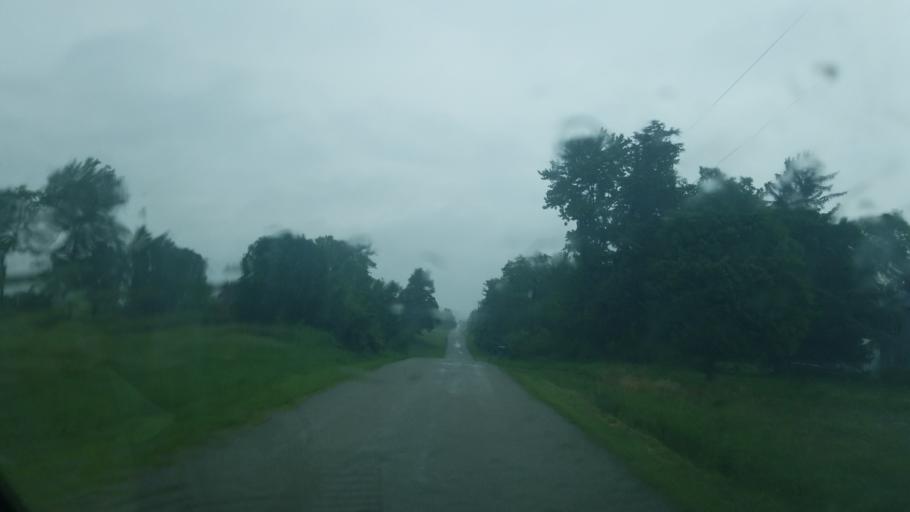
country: US
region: Ohio
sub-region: Richland County
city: Shelby
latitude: 40.9264
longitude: -82.7976
